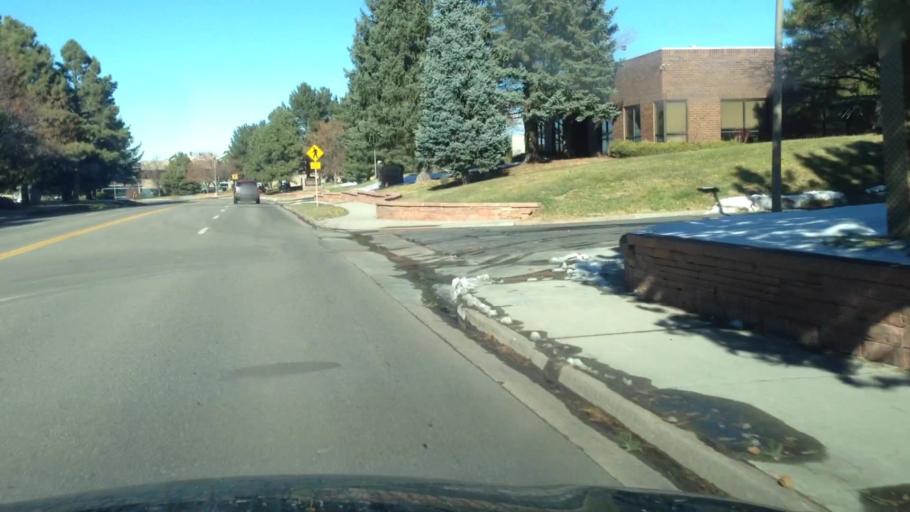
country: US
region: Colorado
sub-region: Douglas County
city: Meridian
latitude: 39.5726
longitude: -104.8562
